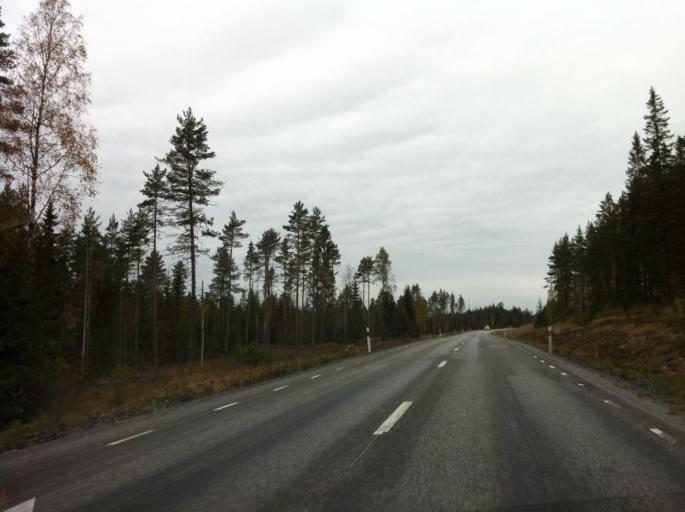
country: SE
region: OErebro
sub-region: Ljusnarsbergs Kommun
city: Kopparberg
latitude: 59.9482
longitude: 15.0213
